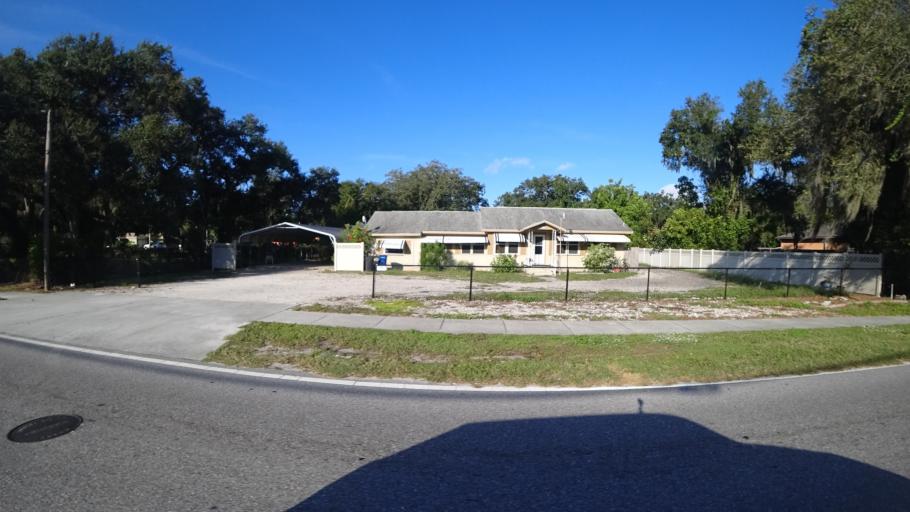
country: US
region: Florida
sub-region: Manatee County
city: West Samoset
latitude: 27.4755
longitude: -82.5548
